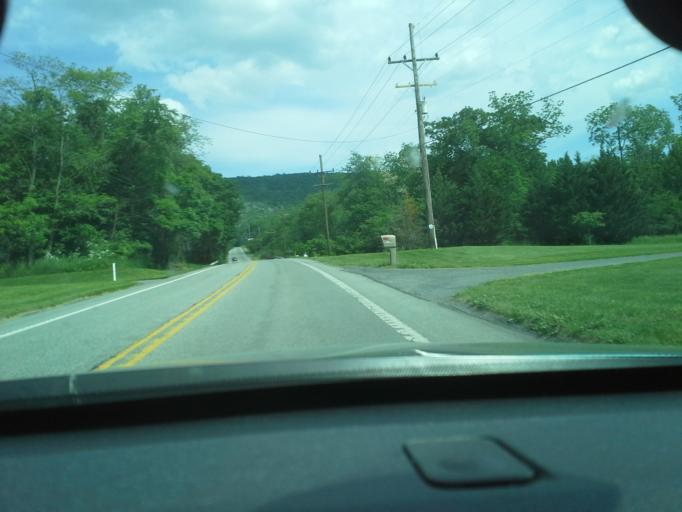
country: US
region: Pennsylvania
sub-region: Fulton County
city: McConnellsburg
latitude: 39.9199
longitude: -77.9782
